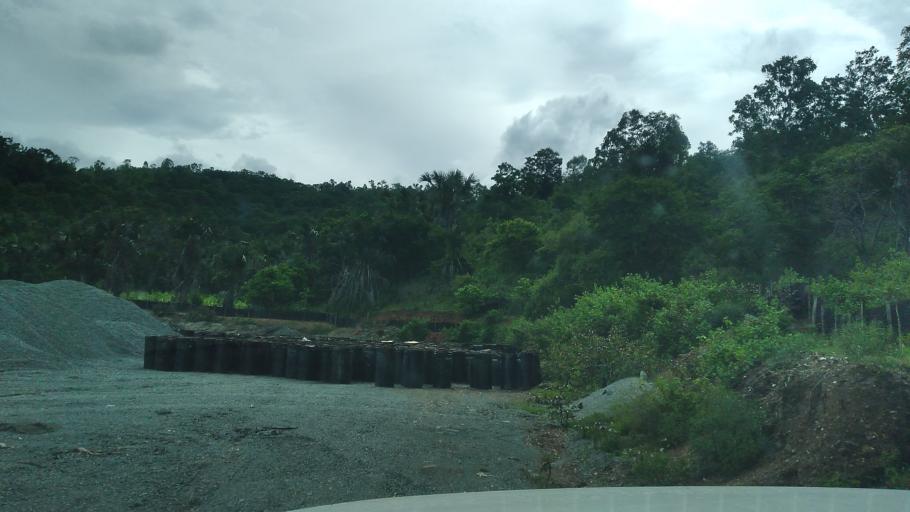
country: TL
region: Dili
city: Dili
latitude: -8.5985
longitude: 125.4767
